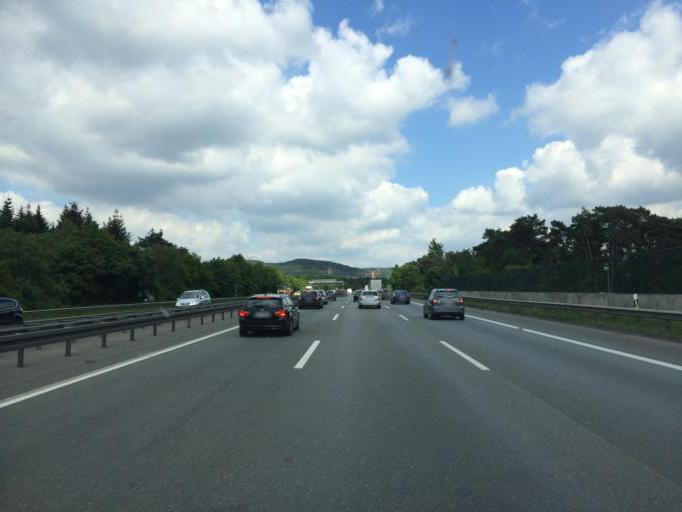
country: DE
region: North Rhine-Westphalia
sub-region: Regierungsbezirk Detmold
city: Bielefeld
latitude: 51.9552
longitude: 8.5712
